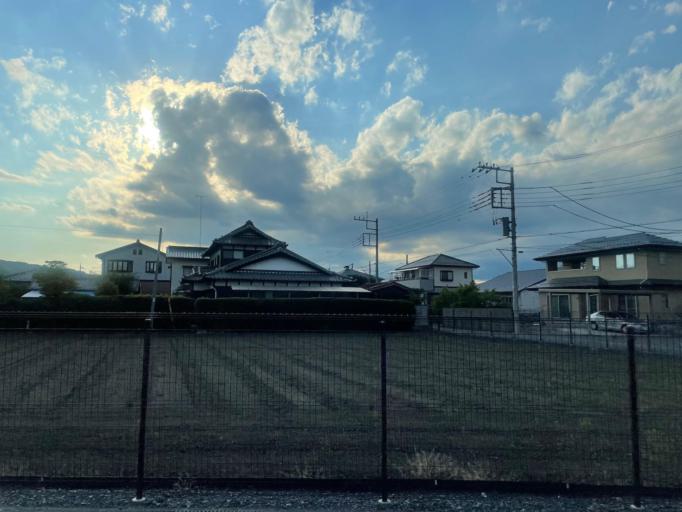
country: JP
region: Tochigi
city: Tochigi
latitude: 36.3729
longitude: 139.7219
